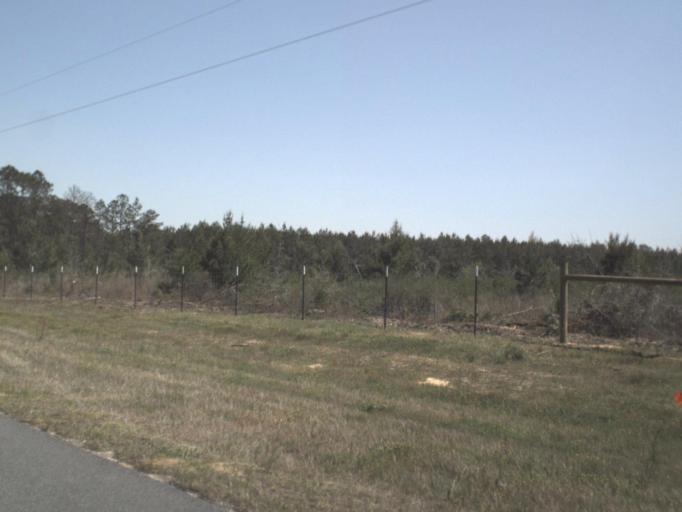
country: US
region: Florida
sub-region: Bay County
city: Youngstown
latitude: 30.4355
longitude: -85.3552
